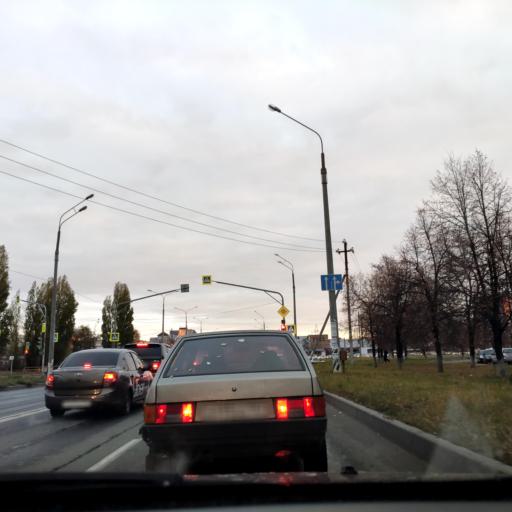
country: RU
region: Samara
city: Tol'yatti
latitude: 53.5413
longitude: 49.3156
